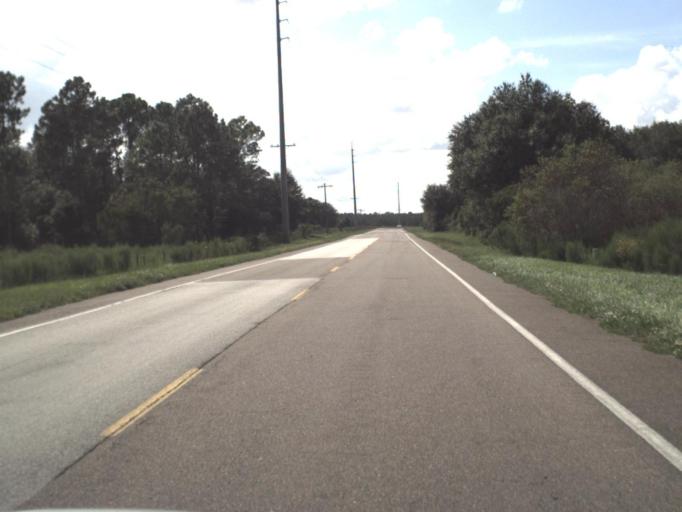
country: US
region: Florida
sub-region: Hardee County
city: Wauchula
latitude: 27.4852
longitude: -81.9518
